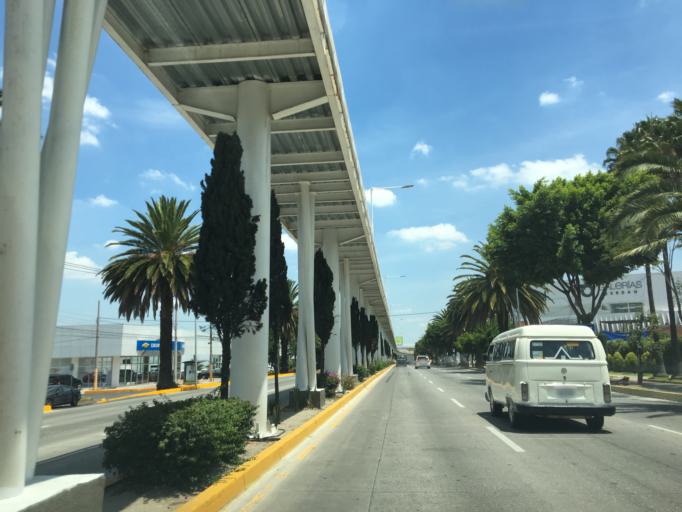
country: MX
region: Puebla
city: Puebla
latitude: 19.0686
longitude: -98.2249
